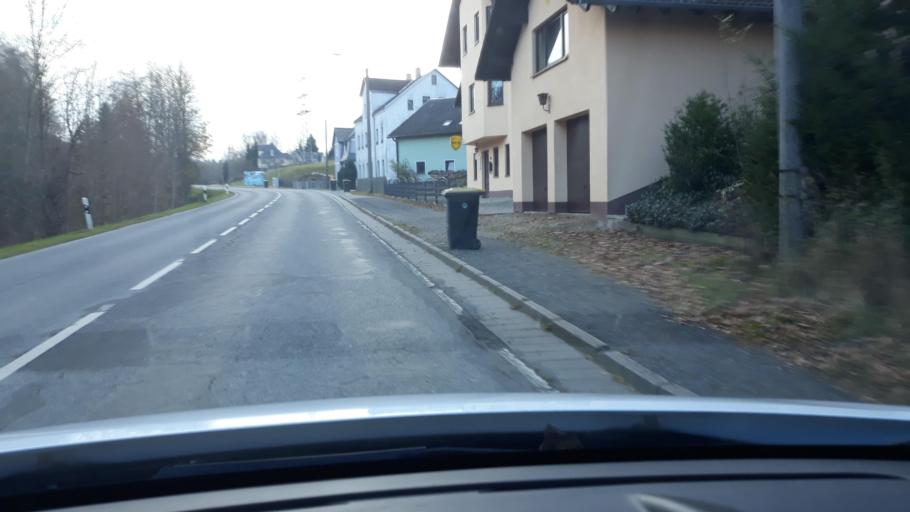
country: DE
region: Saxony
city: Kirchberg
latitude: 50.6366
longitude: 12.5180
